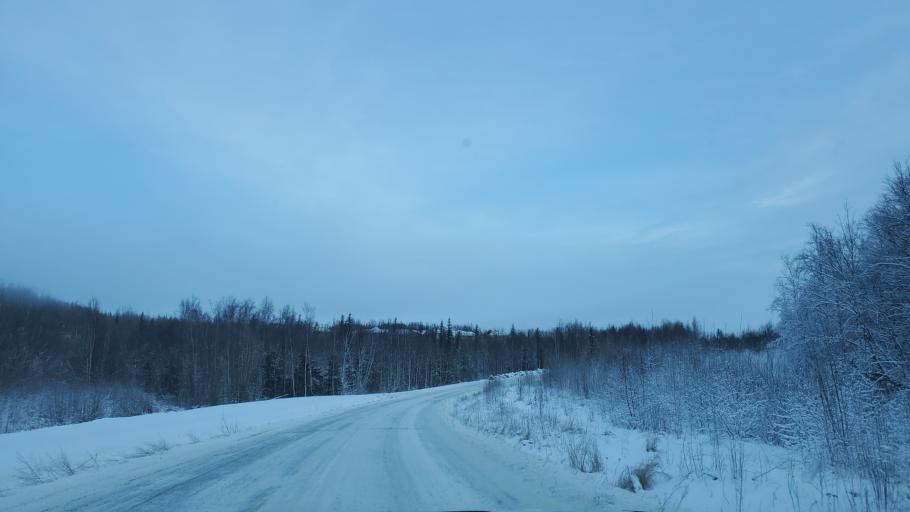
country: US
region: Alaska
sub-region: Matanuska-Susitna Borough
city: Lakes
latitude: 61.5506
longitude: -149.3015
